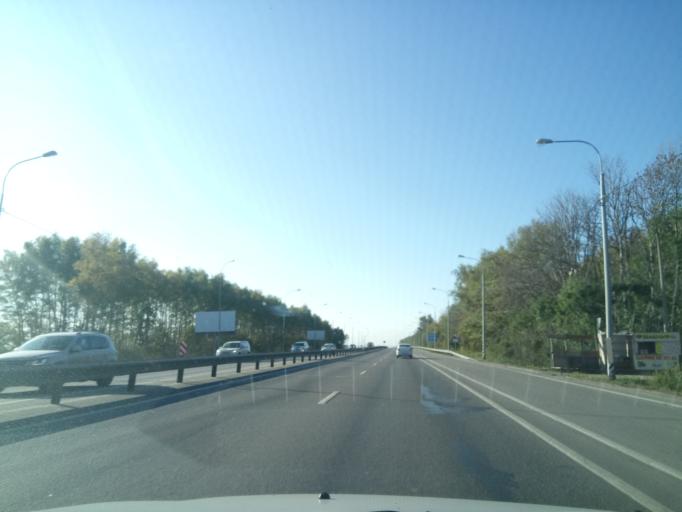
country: RU
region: Nizjnij Novgorod
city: Nizhniy Novgorod
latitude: 56.2085
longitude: 43.9275
